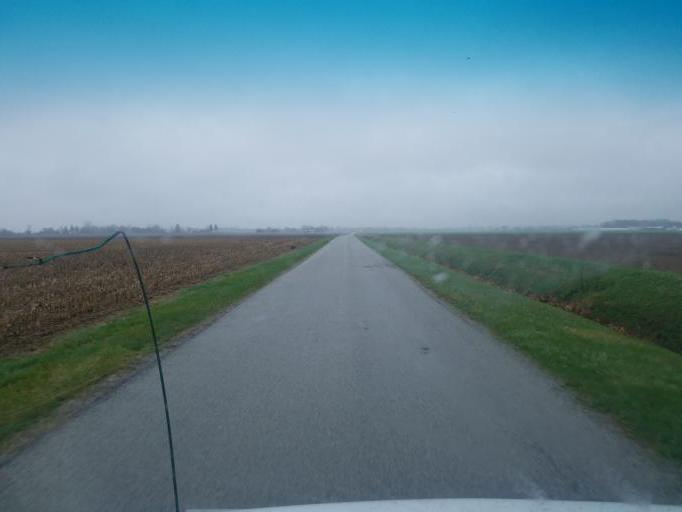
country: US
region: Ohio
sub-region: Wood County
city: North Baltimore
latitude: 41.2631
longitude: -83.6313
